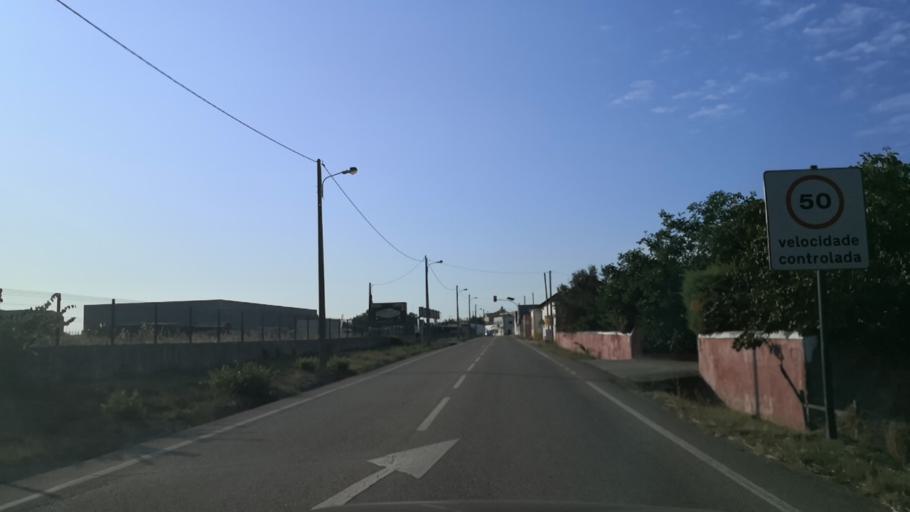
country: PT
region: Santarem
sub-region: Santarem
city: Santarem
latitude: 39.3345
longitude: -8.6610
